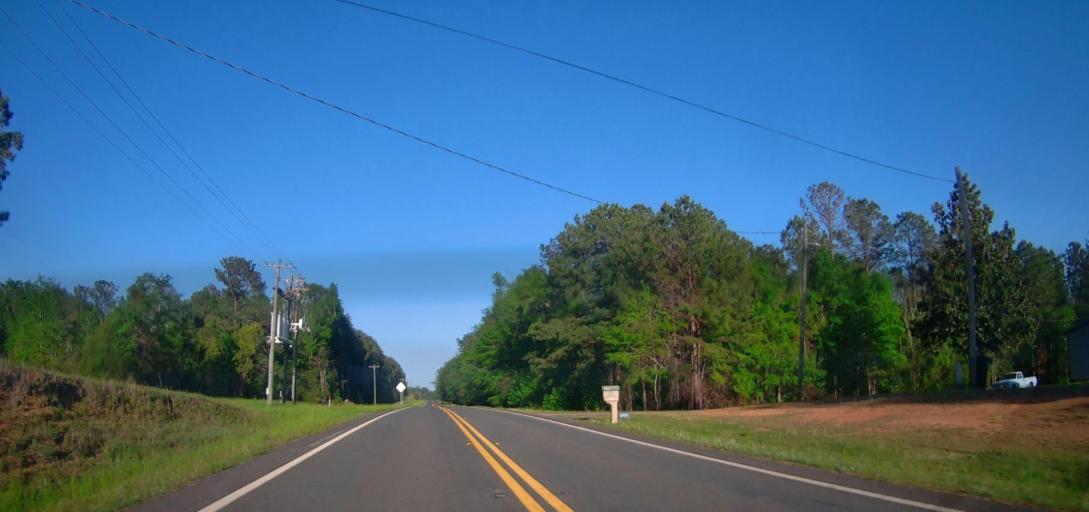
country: US
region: Georgia
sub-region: Schley County
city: Ellaville
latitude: 32.3215
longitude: -84.2192
